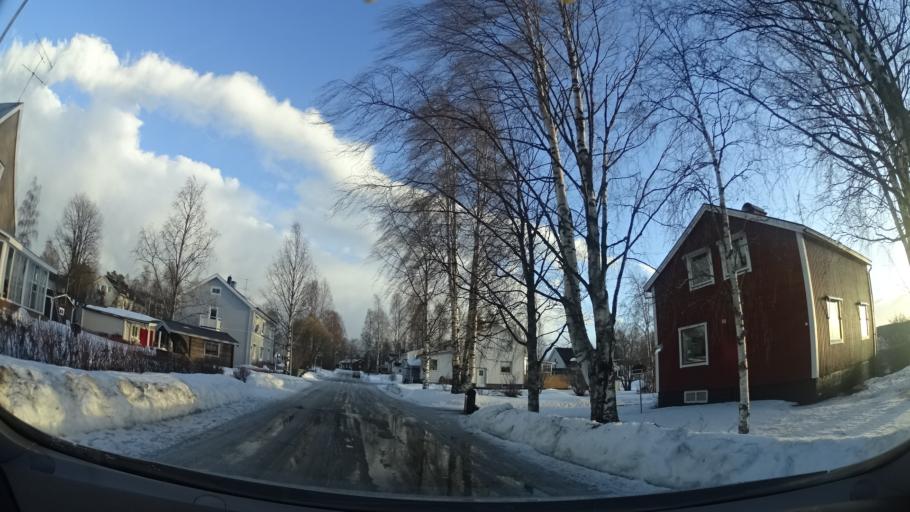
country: SE
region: Vaesterbotten
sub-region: Mala Kommun
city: Mala
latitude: 65.1850
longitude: 18.7364
